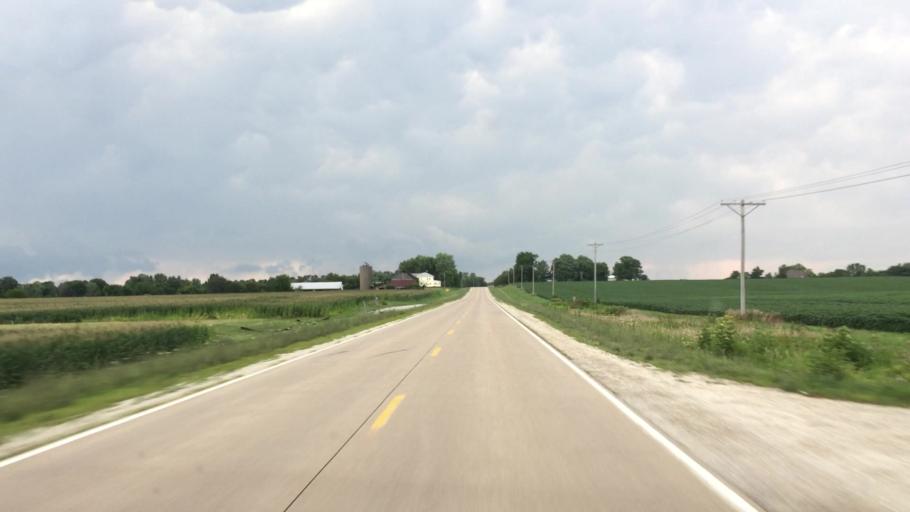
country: US
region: Iowa
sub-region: Lee County
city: Fort Madison
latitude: 40.7253
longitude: -91.3297
